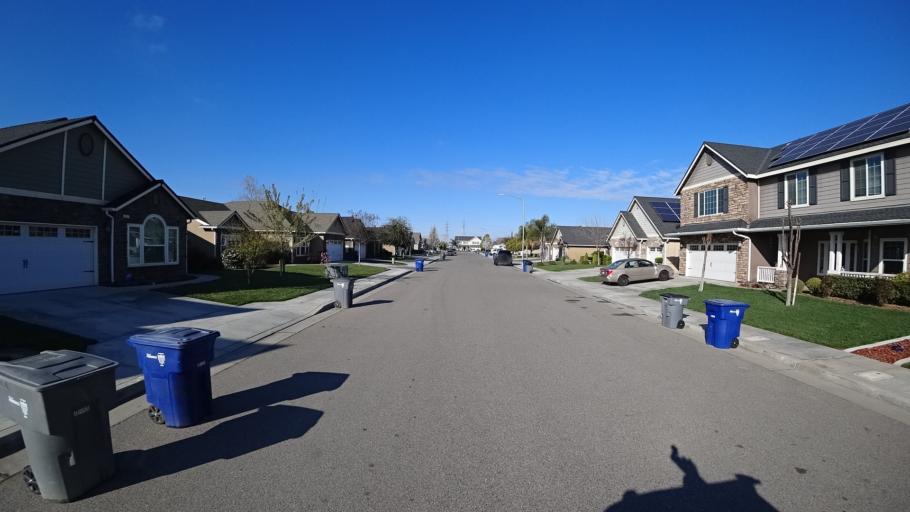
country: US
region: California
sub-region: Fresno County
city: Biola
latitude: 36.8434
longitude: -119.9128
